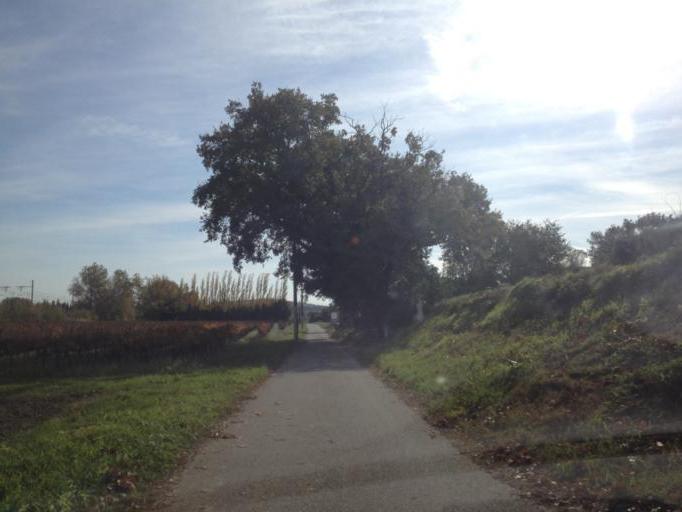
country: FR
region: Provence-Alpes-Cote d'Azur
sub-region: Departement du Vaucluse
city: Bedarrides
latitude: 44.0536
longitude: 4.8930
